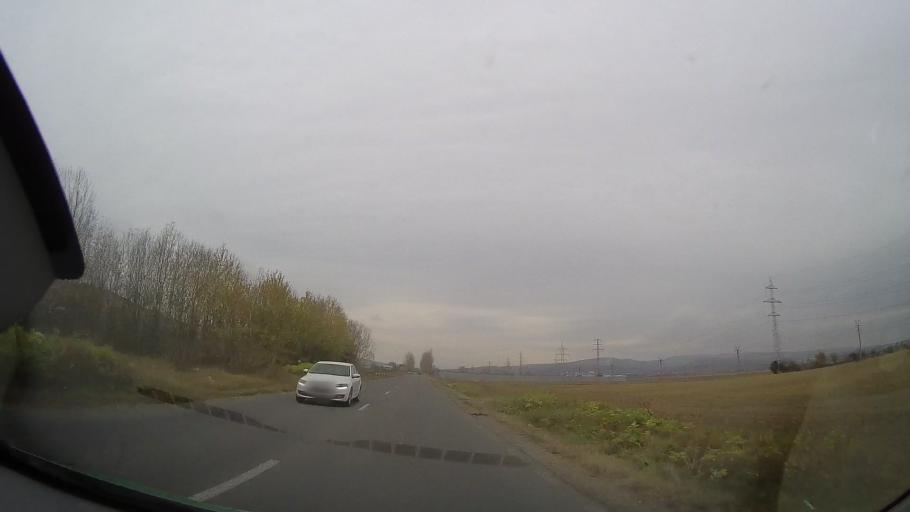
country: RO
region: Prahova
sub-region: Oras Urlati
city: Urlati
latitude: 44.9669
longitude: 26.2344
